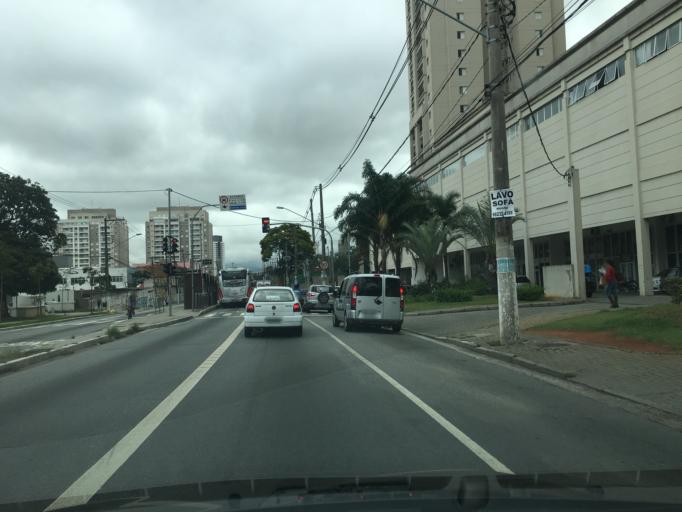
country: BR
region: Sao Paulo
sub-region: Taboao Da Serra
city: Taboao da Serra
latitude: -23.5993
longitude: -46.7415
